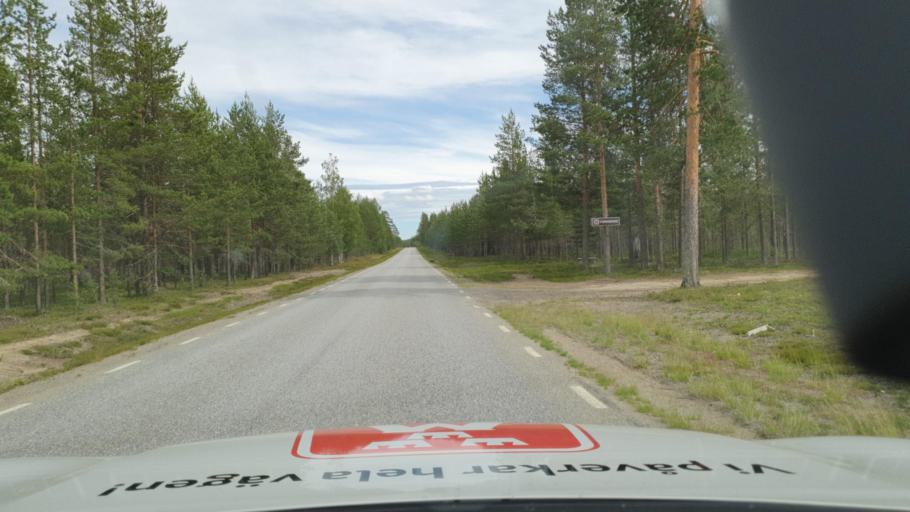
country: SE
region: Vaesterbotten
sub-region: Skelleftea Kommun
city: Burtraesk
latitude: 64.5046
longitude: 20.8111
